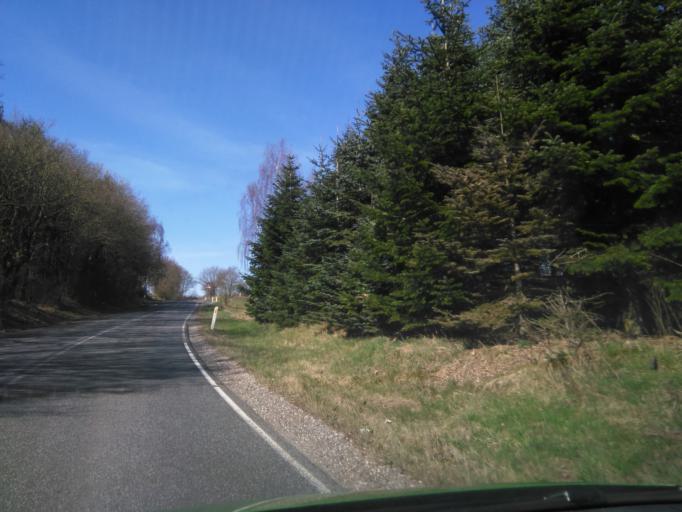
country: DK
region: Central Jutland
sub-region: Skanderborg Kommune
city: Ry
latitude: 56.0217
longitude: 9.7836
